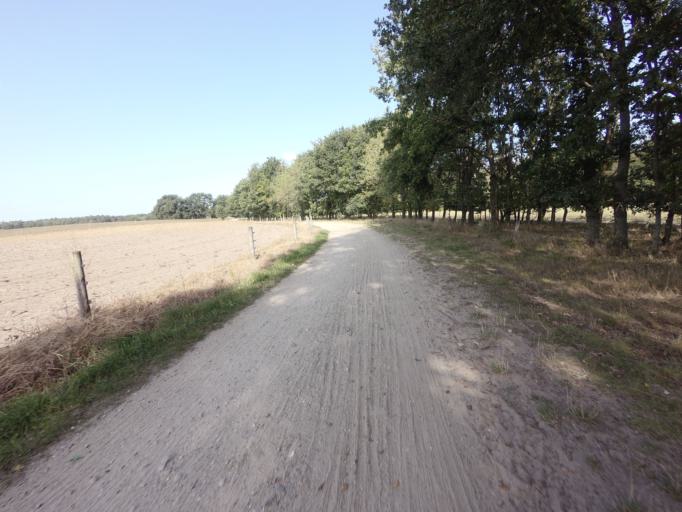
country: NL
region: Limburg
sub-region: Gemeente Roerdalen
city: Herkenbosch
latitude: 51.1706
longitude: 6.0837
